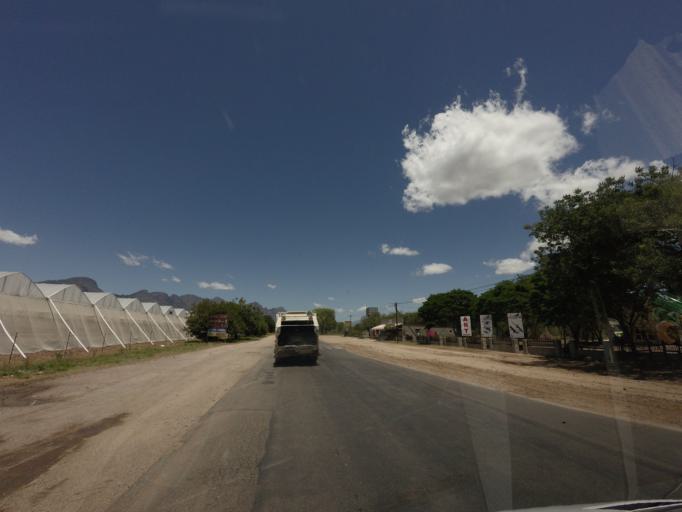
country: ZA
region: Limpopo
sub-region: Mopani District Municipality
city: Hoedspruit
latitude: -24.3962
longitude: 30.8174
